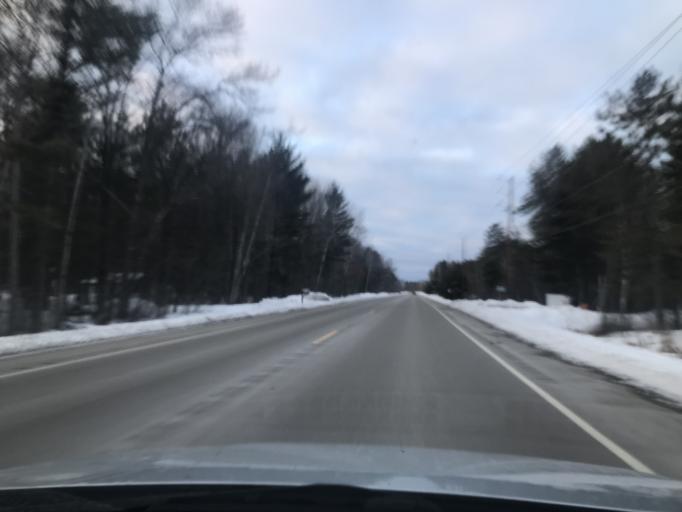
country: US
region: Wisconsin
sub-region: Marinette County
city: Marinette
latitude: 45.1327
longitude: -87.6881
